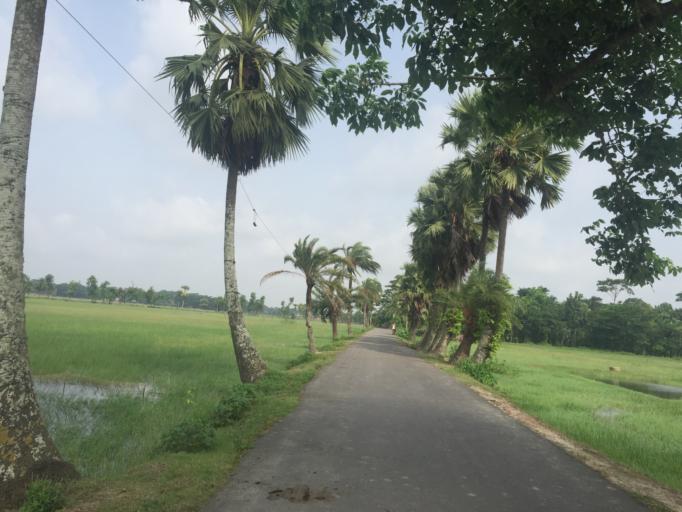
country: BD
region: Barisal
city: Mathba
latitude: 22.2114
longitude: 89.9257
